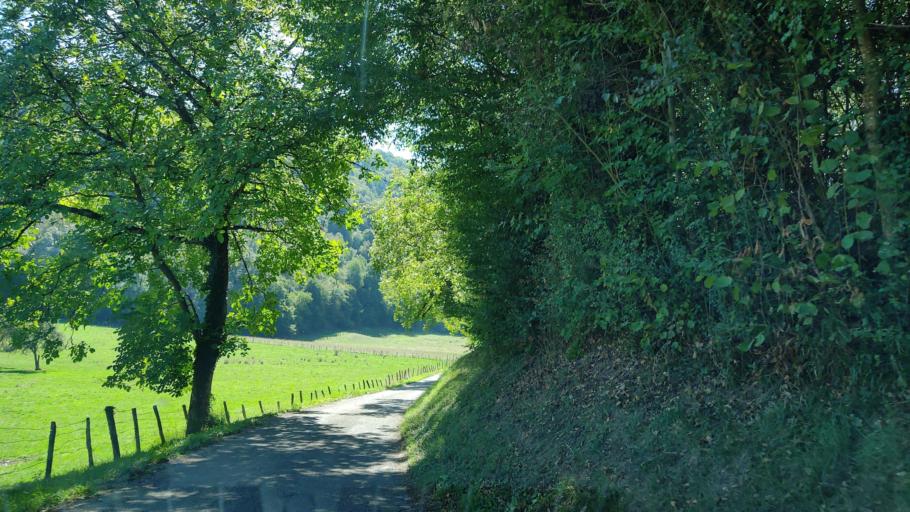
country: FR
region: Rhone-Alpes
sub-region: Departement de la Savoie
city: La Bridoire
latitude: 45.5344
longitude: 5.7537
